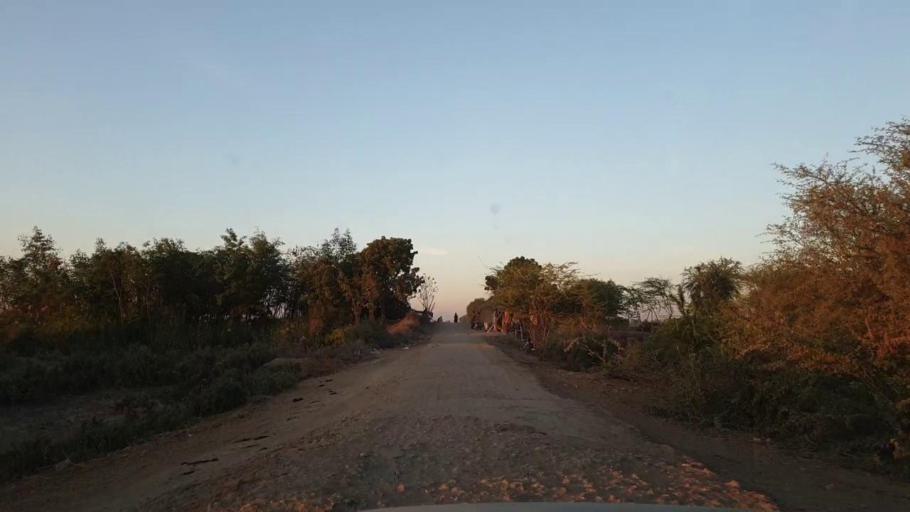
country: PK
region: Sindh
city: Kunri
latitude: 25.1459
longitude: 69.4456
